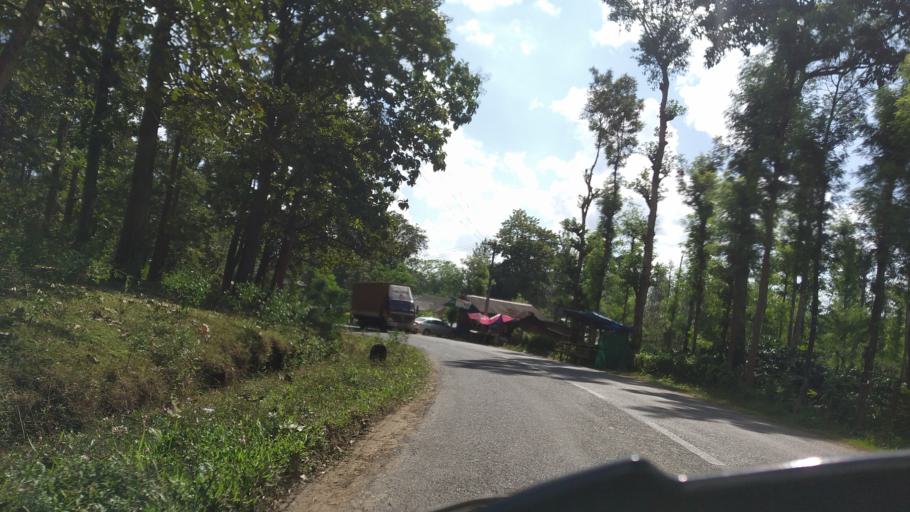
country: IN
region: Kerala
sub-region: Wayanad
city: Panamaram
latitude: 11.9418
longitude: 76.0639
